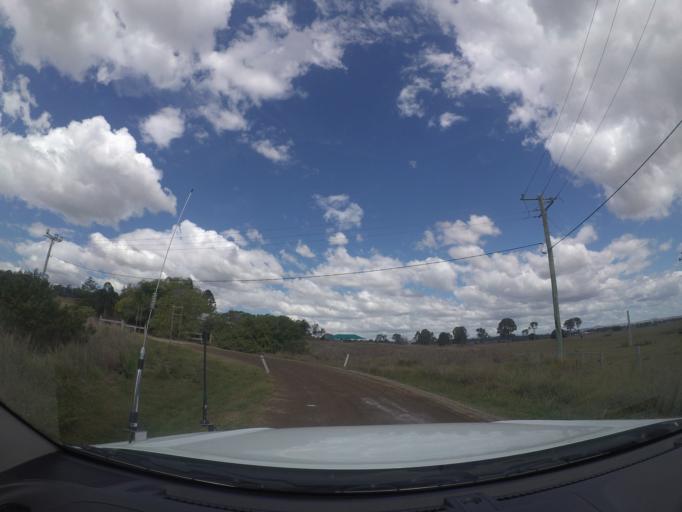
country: AU
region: Queensland
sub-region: Logan
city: Cedar Vale
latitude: -27.9074
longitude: 152.9766
